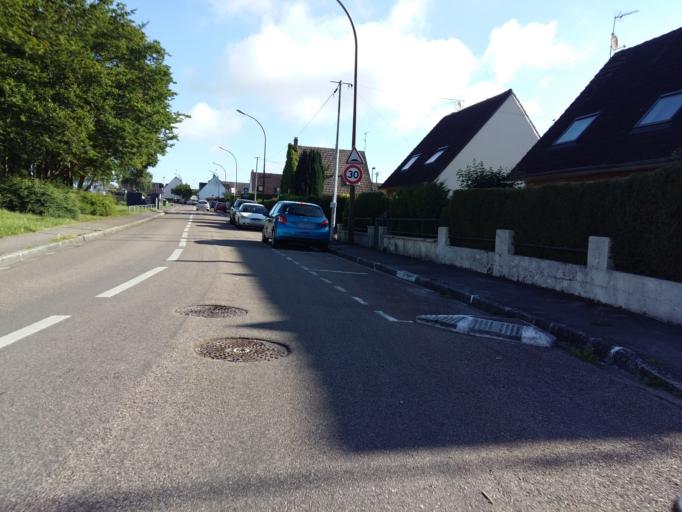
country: FR
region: Picardie
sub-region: Departement de la Somme
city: Rivery
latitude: 49.9119
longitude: 2.3267
